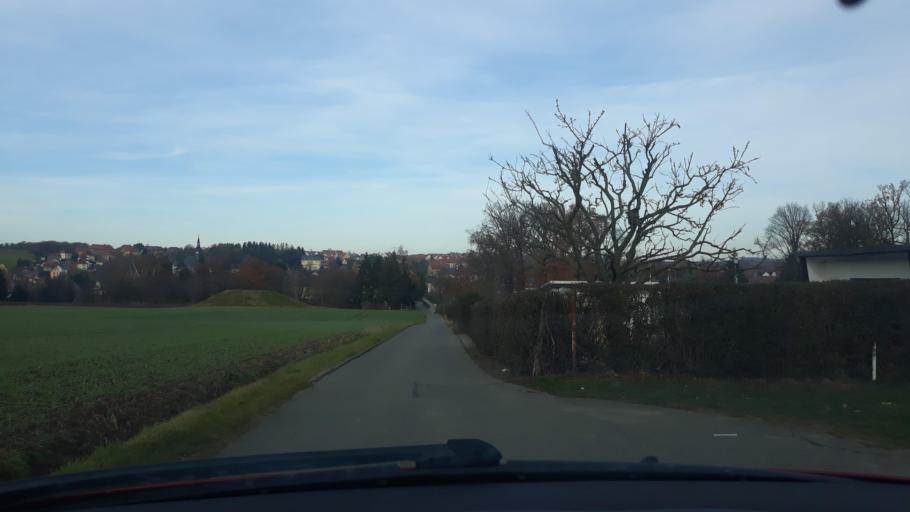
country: DE
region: Saxony
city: Wilkau-Hasslau
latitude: 50.6791
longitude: 12.5494
